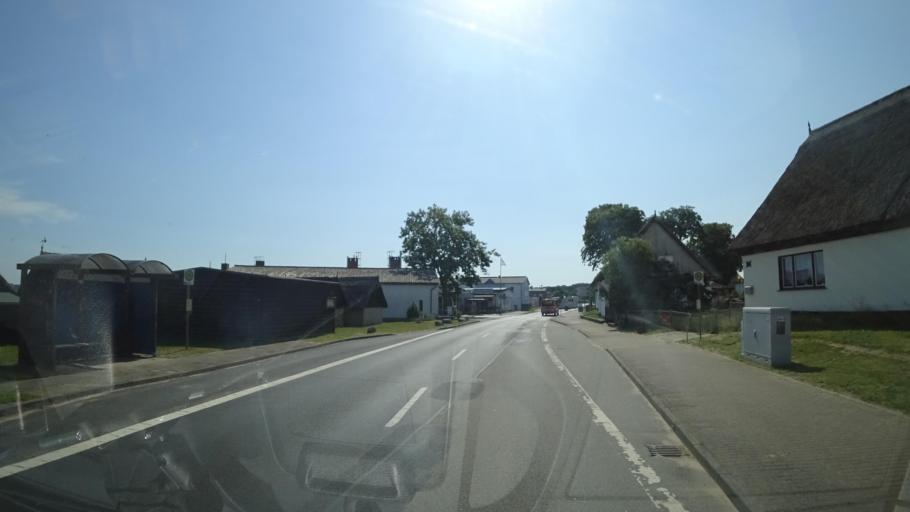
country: DE
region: Mecklenburg-Vorpommern
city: Kroslin
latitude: 54.1366
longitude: 13.7275
